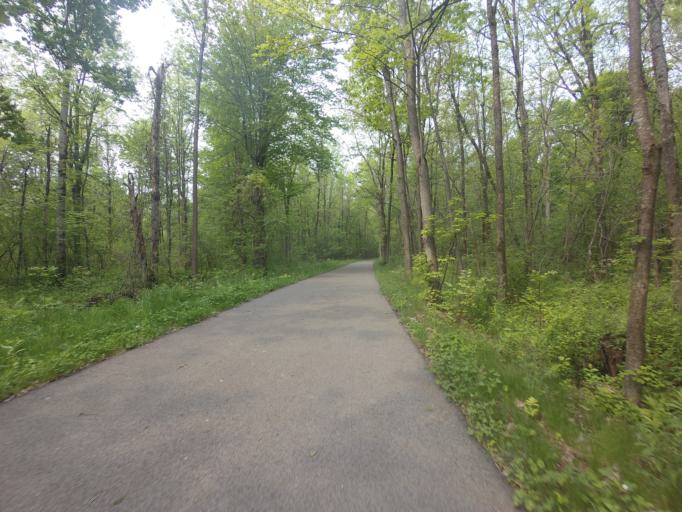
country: US
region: New York
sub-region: Jefferson County
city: Watertown
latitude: 43.9724
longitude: -75.8649
